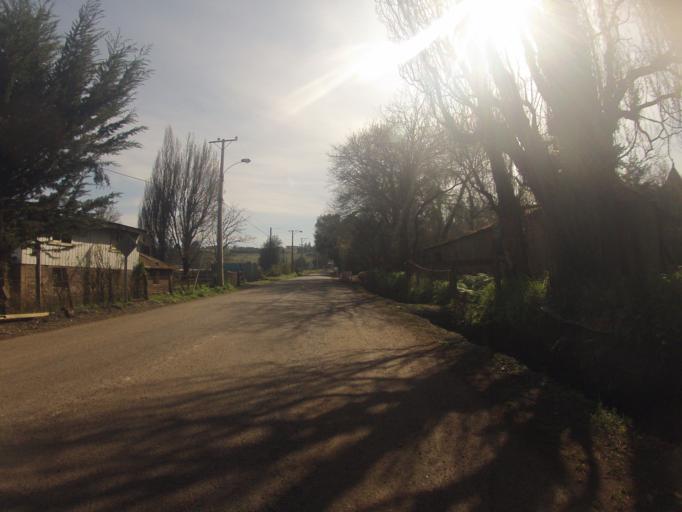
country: CL
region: Araucania
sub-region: Provincia de Cautin
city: Temuco
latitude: -38.7115
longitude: -72.5993
